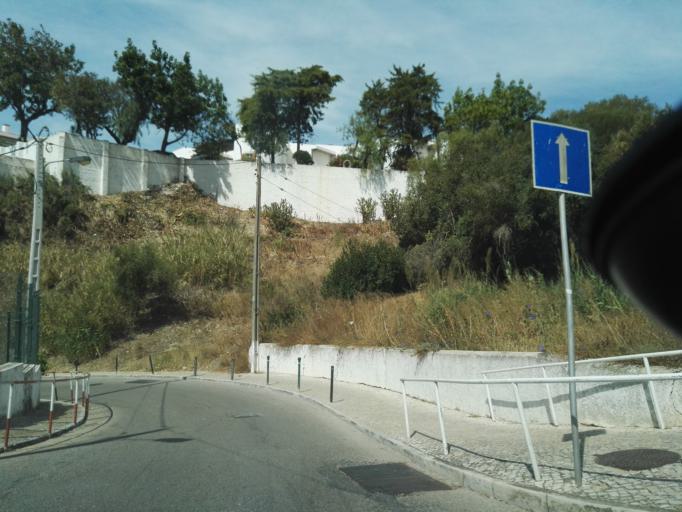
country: PT
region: Setubal
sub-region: Sesimbra
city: Sesimbra
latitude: 38.4455
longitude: -9.0979
